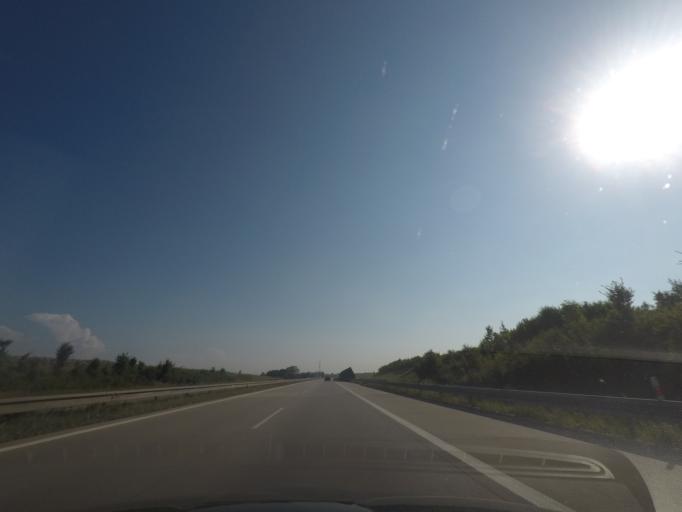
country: CZ
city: Bilovec
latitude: 49.7160
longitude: 18.0038
